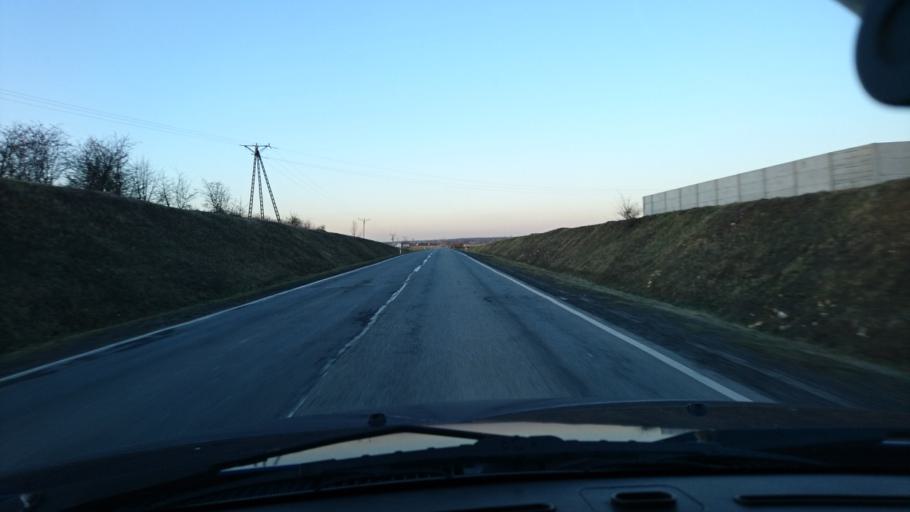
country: PL
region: Silesian Voivodeship
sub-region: Powiat gliwicki
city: Wielowies
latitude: 50.5077
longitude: 18.6046
